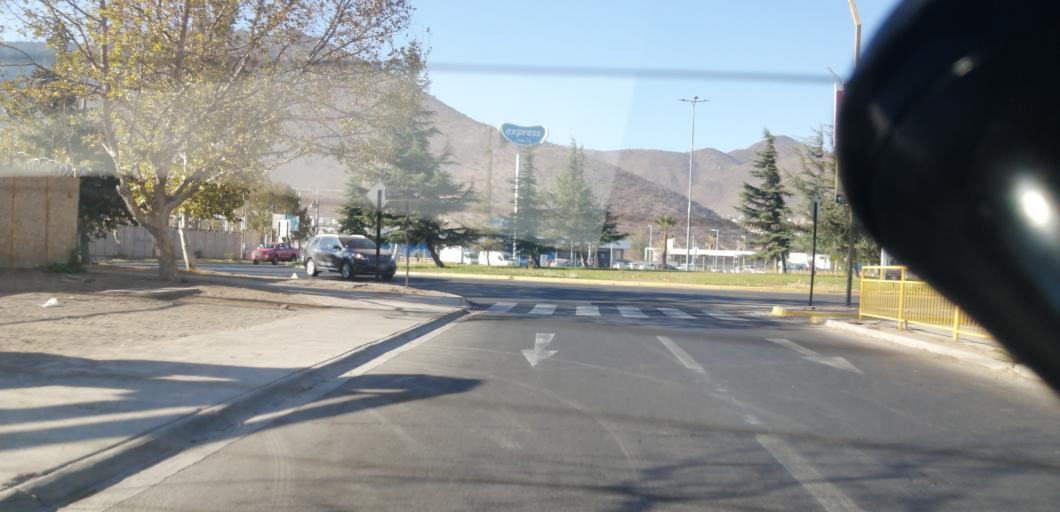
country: CL
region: Santiago Metropolitan
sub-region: Provincia de Santiago
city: Lo Prado
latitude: -33.4465
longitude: -70.8451
